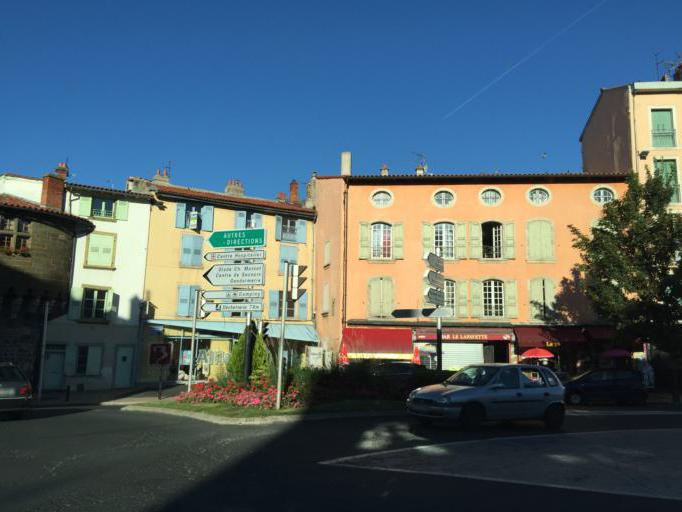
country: FR
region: Auvergne
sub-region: Departement de la Haute-Loire
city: Le Puy-en-Velay
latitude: 45.0443
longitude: 3.8799
